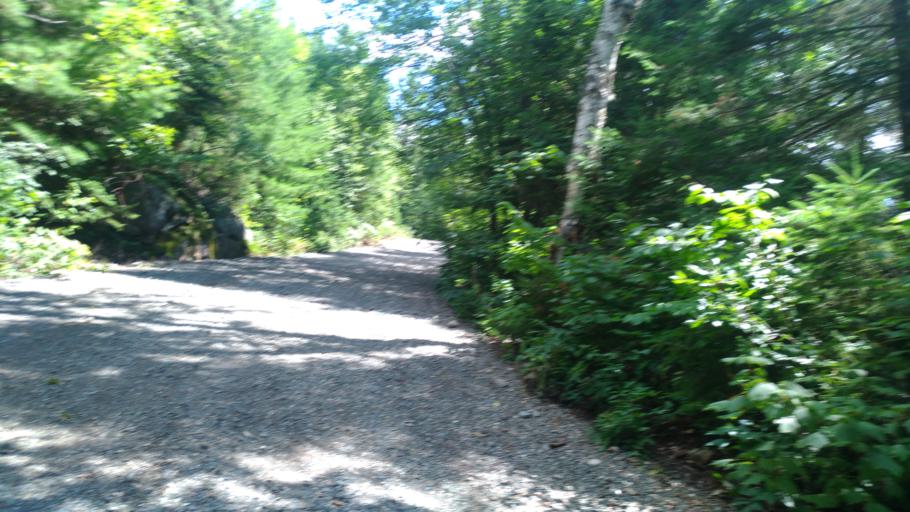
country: CA
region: Ontario
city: Rayside-Balfour
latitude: 46.5917
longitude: -81.5506
